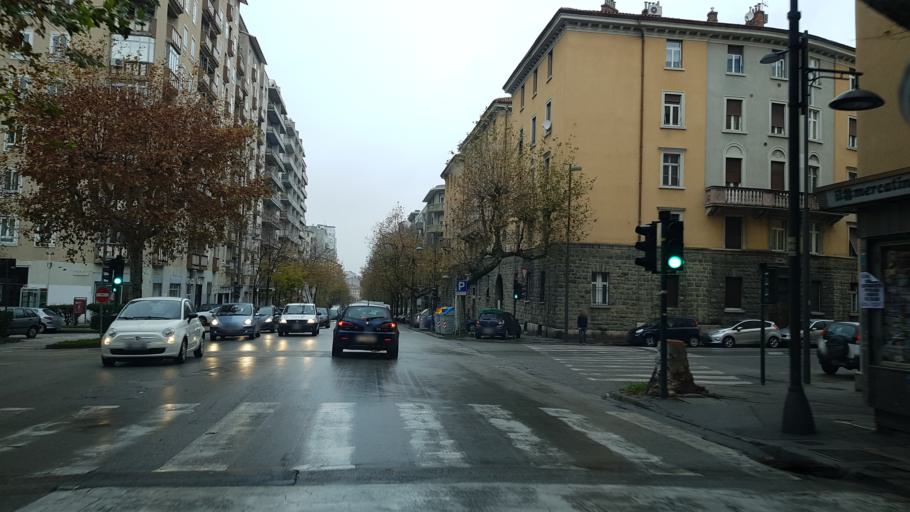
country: IT
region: Friuli Venezia Giulia
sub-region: Provincia di Trieste
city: Trieste
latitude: 45.6421
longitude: 13.7854
